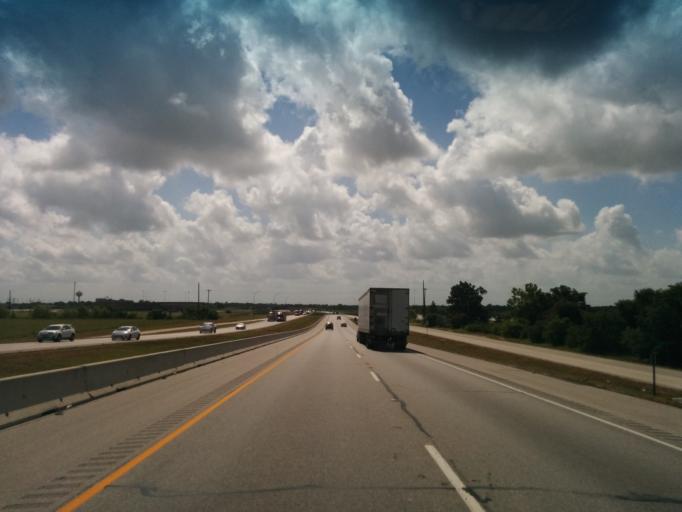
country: US
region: Texas
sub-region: Austin County
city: Sealy
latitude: 29.7622
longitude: -96.1830
